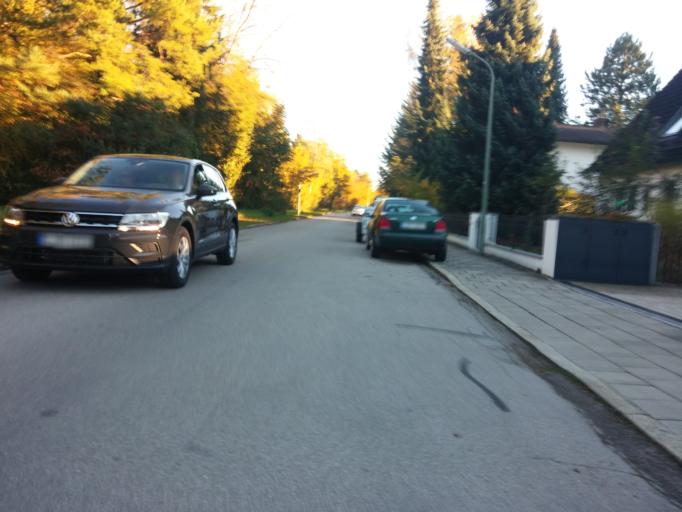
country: DE
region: Bavaria
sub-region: Upper Bavaria
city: Haar
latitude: 48.1048
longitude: 11.7026
